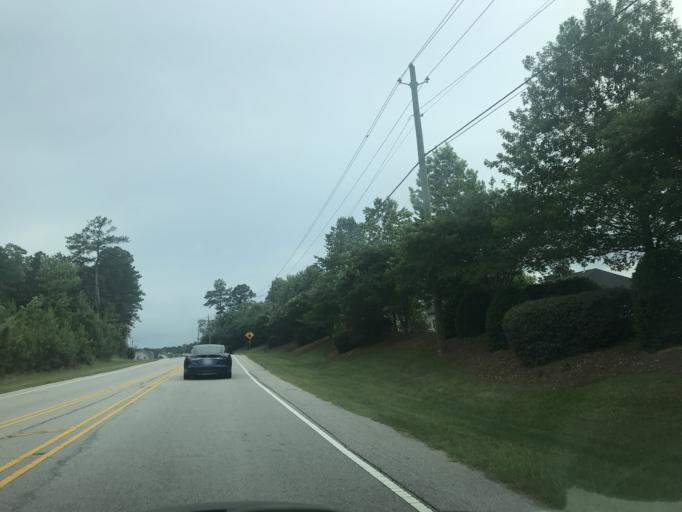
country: US
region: North Carolina
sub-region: Wake County
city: Green Level
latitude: 35.7996
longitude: -78.8978
